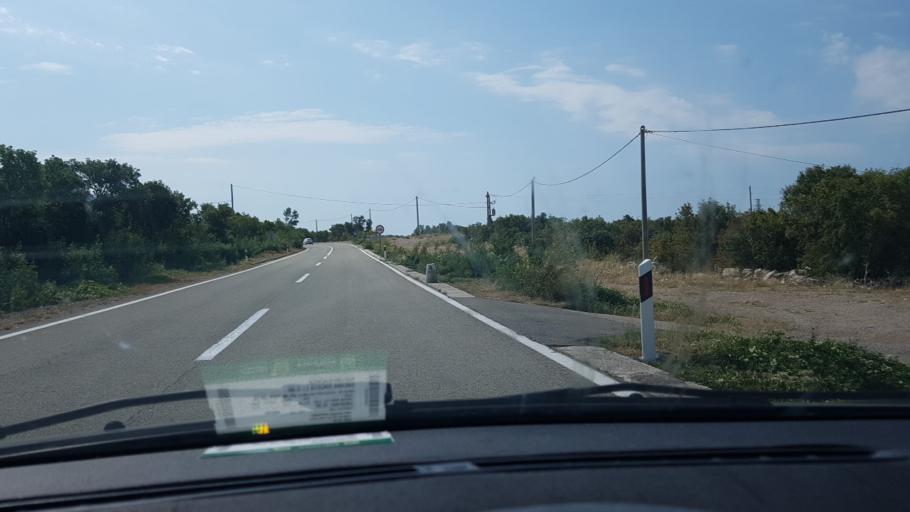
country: HR
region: Licko-Senjska
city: Novalja
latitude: 44.6946
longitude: 14.9226
